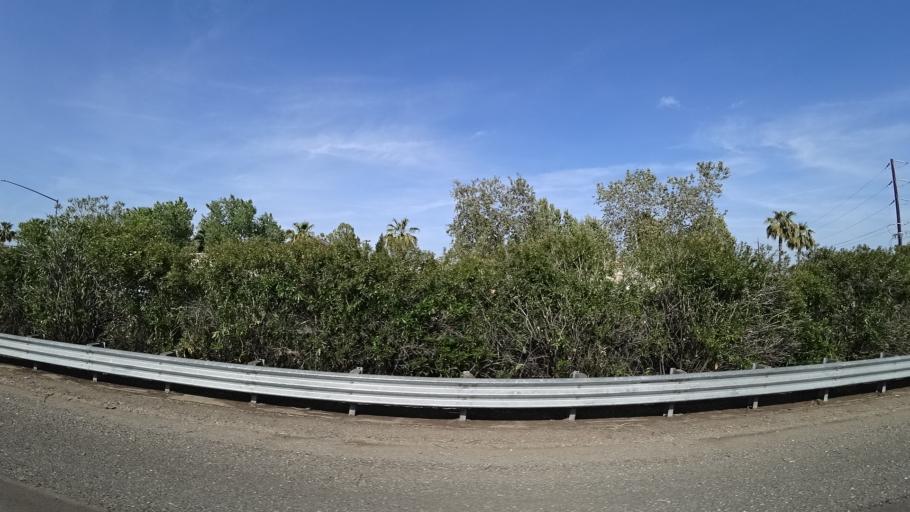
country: US
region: California
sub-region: Butte County
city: Chico
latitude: 39.7227
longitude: -121.8068
